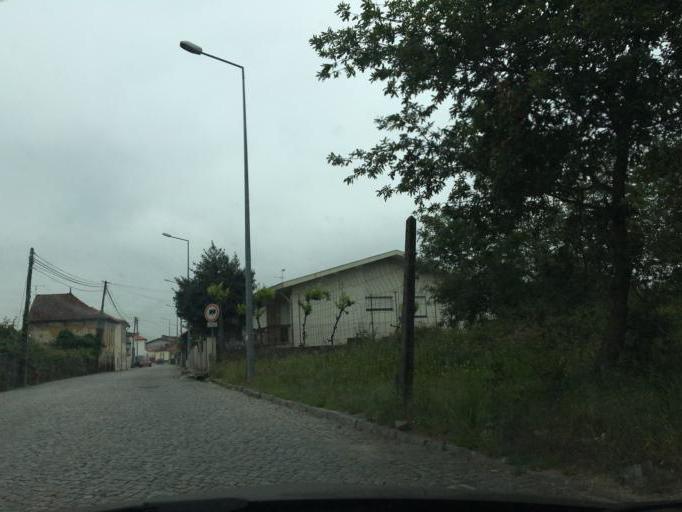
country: PT
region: Porto
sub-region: Maia
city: Nogueira
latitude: 41.2417
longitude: -8.5990
